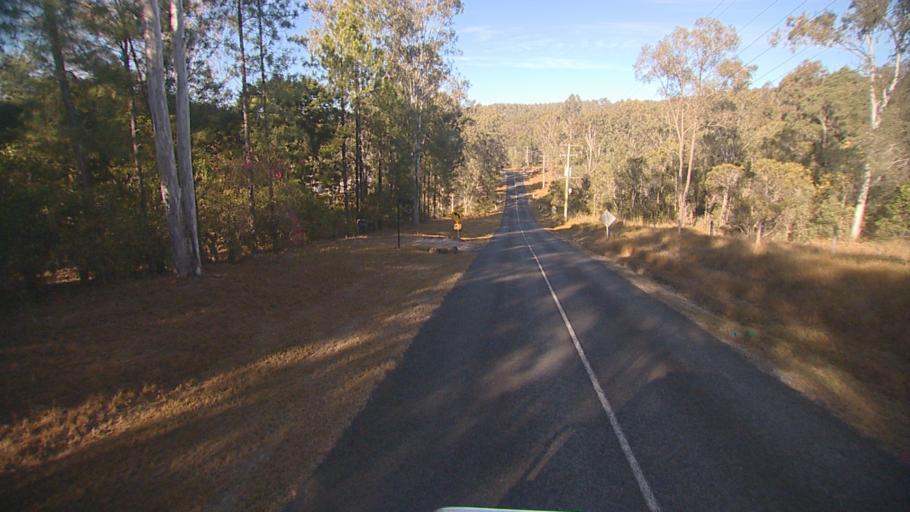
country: AU
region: Queensland
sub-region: Logan
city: Cedar Vale
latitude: -27.8415
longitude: 153.0830
